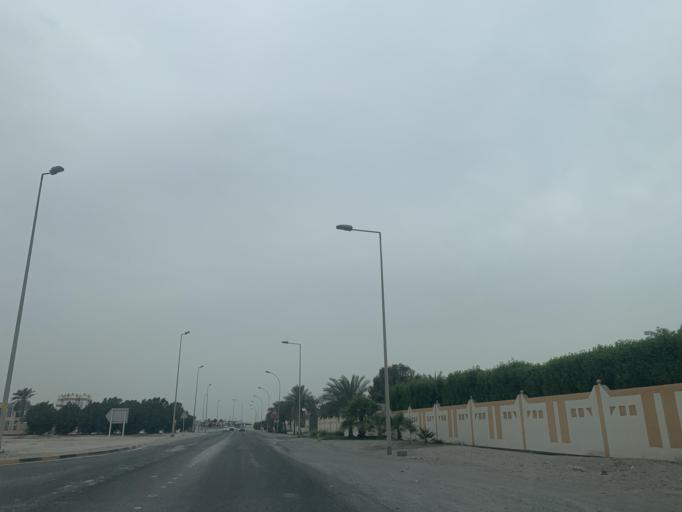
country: BH
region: Muharraq
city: Al Hadd
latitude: 26.2114
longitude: 50.6615
